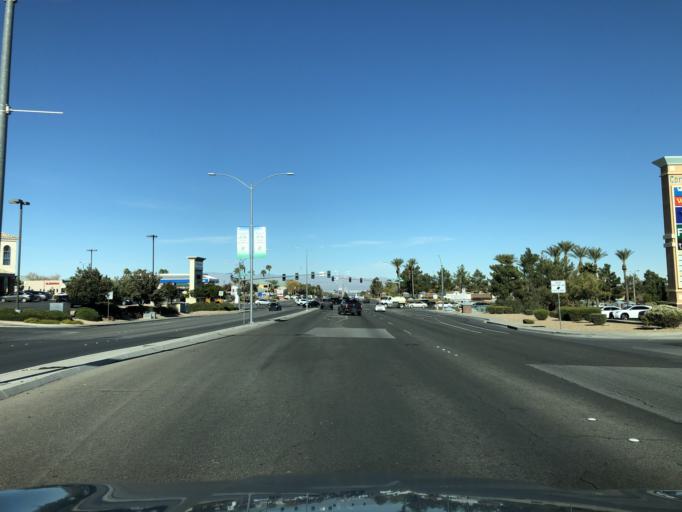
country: US
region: Nevada
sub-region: Clark County
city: Whitney
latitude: 36.0046
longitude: -115.0832
